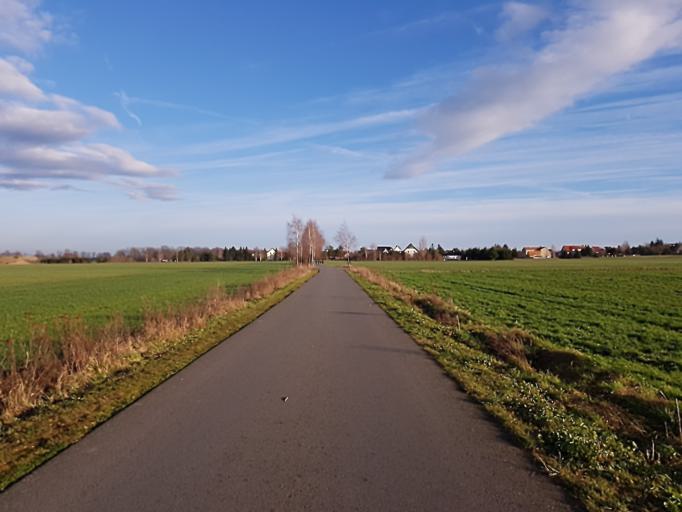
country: DE
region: Brandenburg
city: Groden
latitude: 51.4073
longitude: 13.5565
